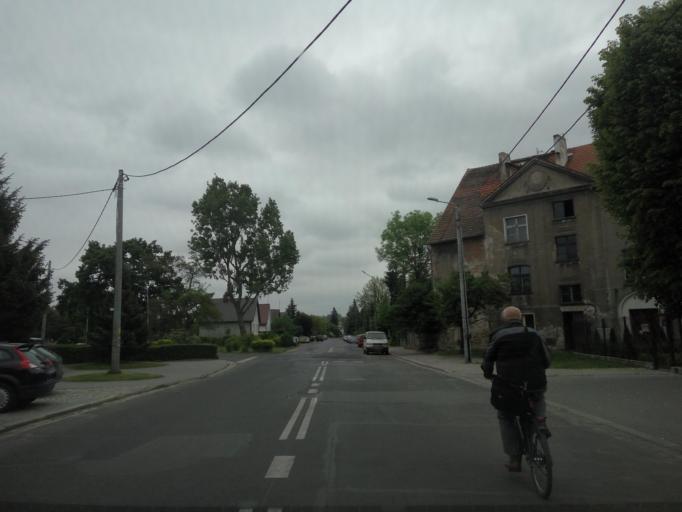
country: PL
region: Lower Silesian Voivodeship
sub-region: Powiat wroclawski
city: Wroclaw
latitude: 51.0998
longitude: 17.0678
